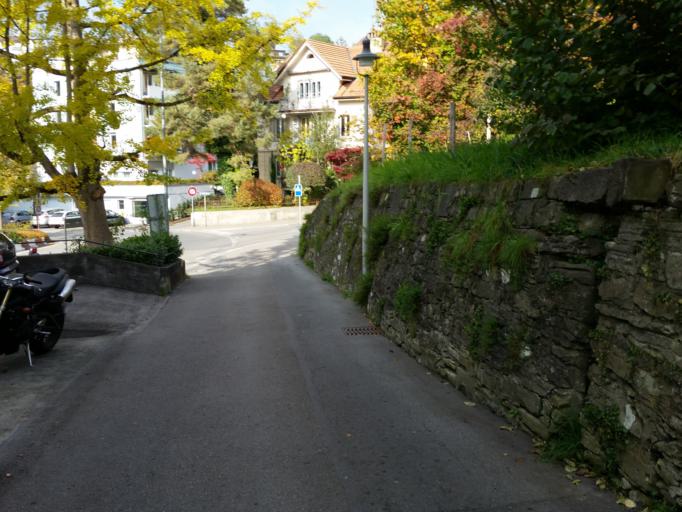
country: CH
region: Lucerne
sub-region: Lucerne-Stadt District
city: Luzern
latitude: 47.0536
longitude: 8.2996
